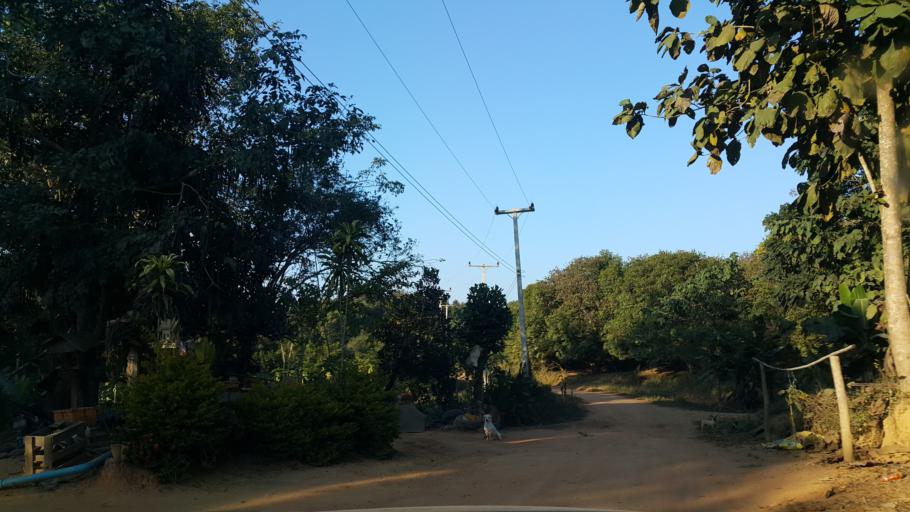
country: TH
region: Sukhothai
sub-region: Amphoe Si Satchanalai
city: Si Satchanalai
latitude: 17.5914
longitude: 99.6158
